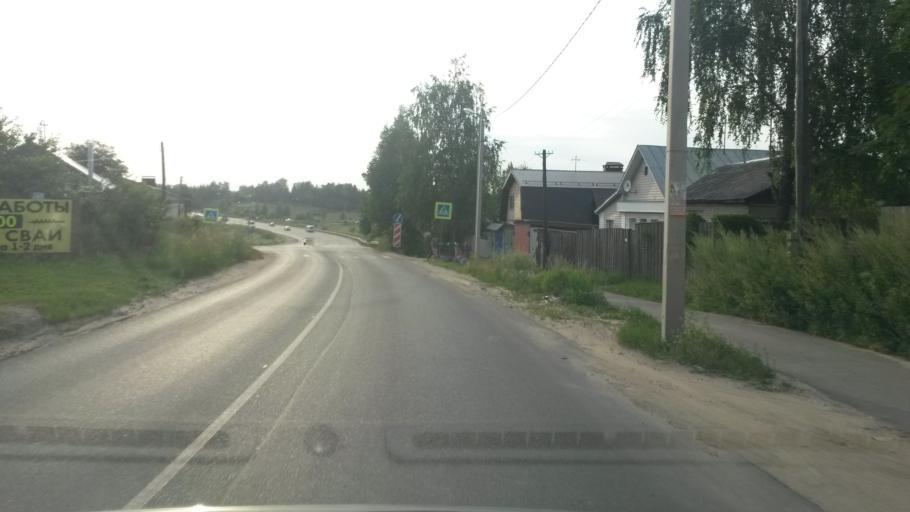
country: RU
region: Ivanovo
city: Novo-Talitsy
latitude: 57.0210
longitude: 40.9136
